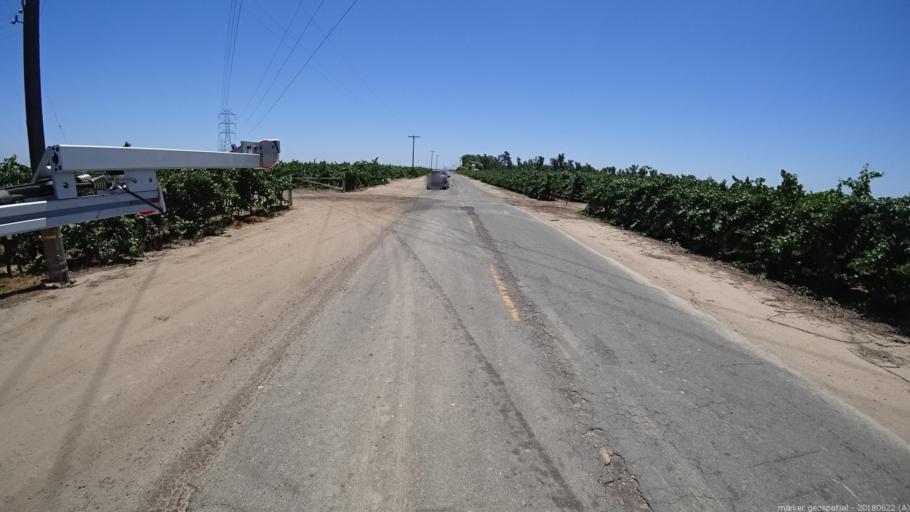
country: US
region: California
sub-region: Madera County
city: Parksdale
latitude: 36.9339
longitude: -119.9922
